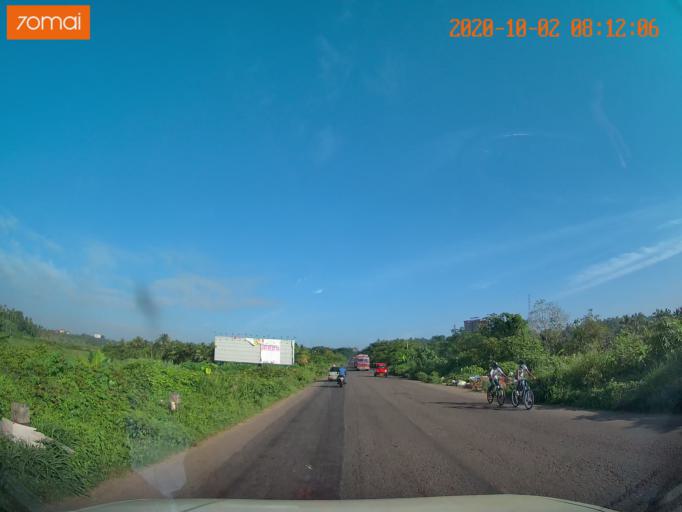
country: IN
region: Kerala
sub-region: Kozhikode
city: Kozhikode
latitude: 11.2787
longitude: 75.8051
